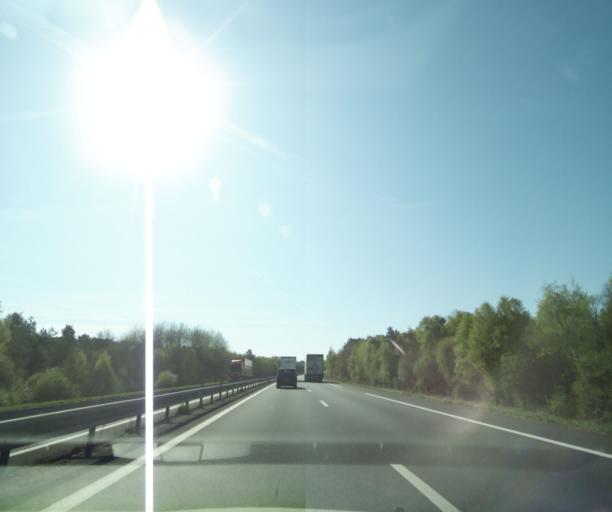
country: FR
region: Centre
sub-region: Departement du Loiret
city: La Ferte-Saint-Aubin
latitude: 47.7154
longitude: 1.8966
